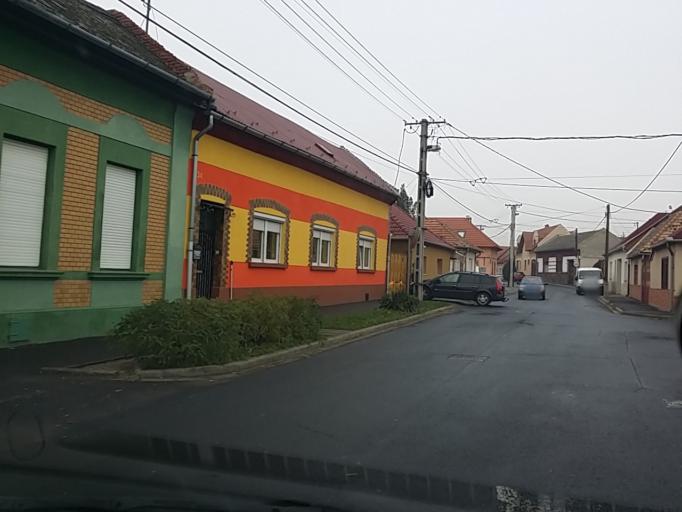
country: HU
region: Heves
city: Gyongyos
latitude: 47.7889
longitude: 19.9297
